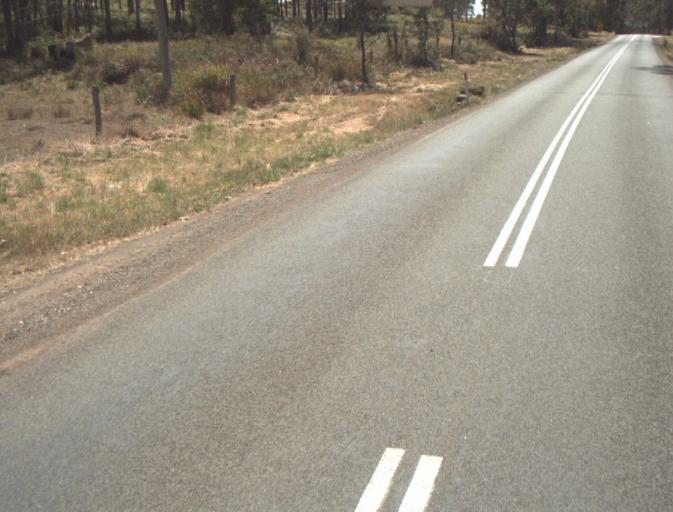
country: AU
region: Tasmania
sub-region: Launceston
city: Mayfield
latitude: -41.2813
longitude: 147.1261
